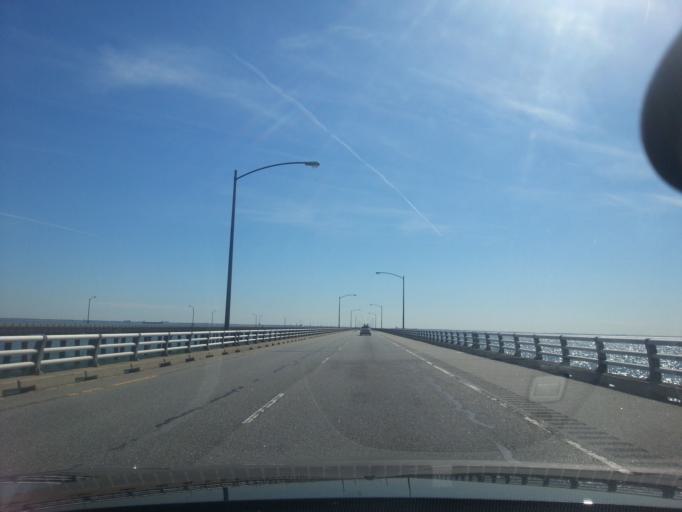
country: US
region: Virginia
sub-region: City of Virginia Beach
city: Virginia Beach
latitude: 37.0211
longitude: -76.0909
